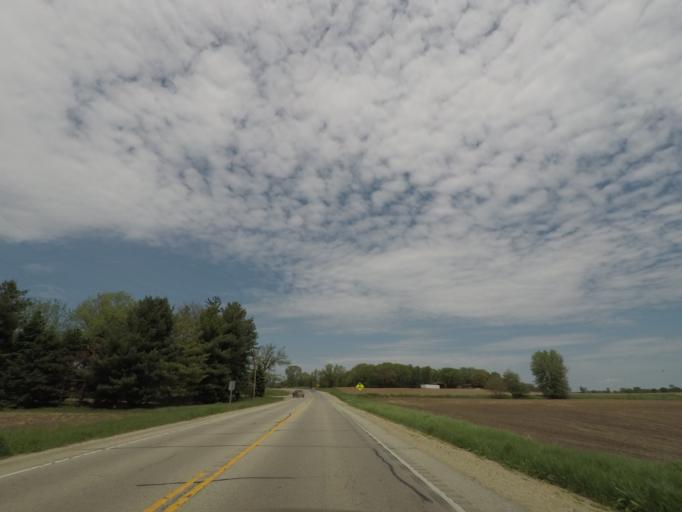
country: US
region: Wisconsin
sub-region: Rock County
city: Evansville
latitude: 42.8160
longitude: -89.2991
